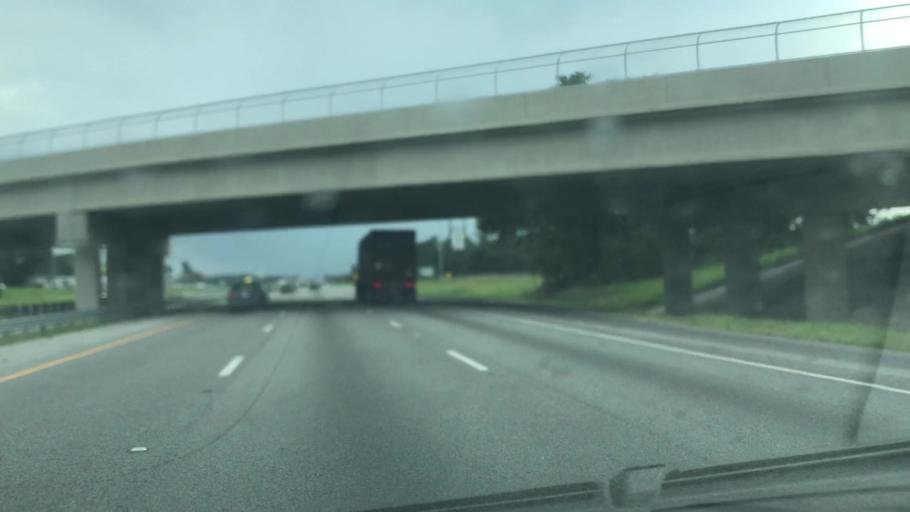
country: US
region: Georgia
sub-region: McIntosh County
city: Darien
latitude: 31.3959
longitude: -81.4498
